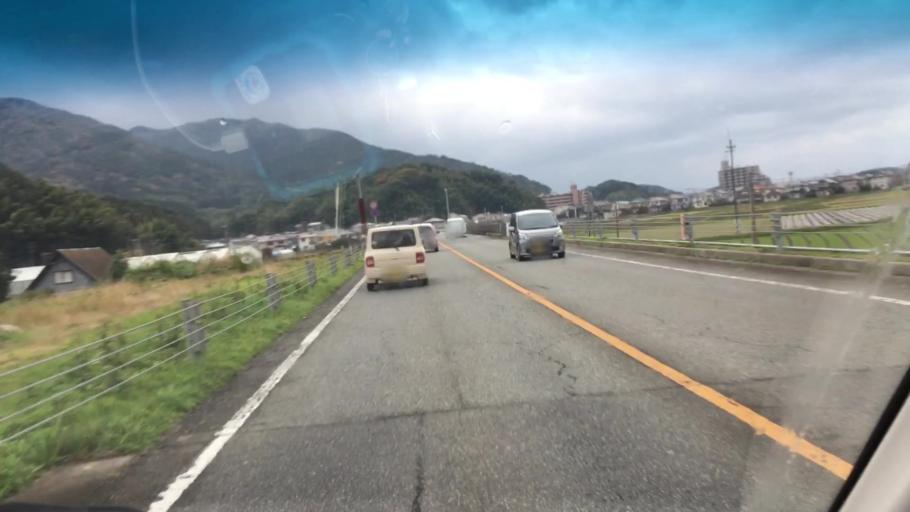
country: JP
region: Fukuoka
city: Maebaru-chuo
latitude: 33.5141
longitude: 130.1474
